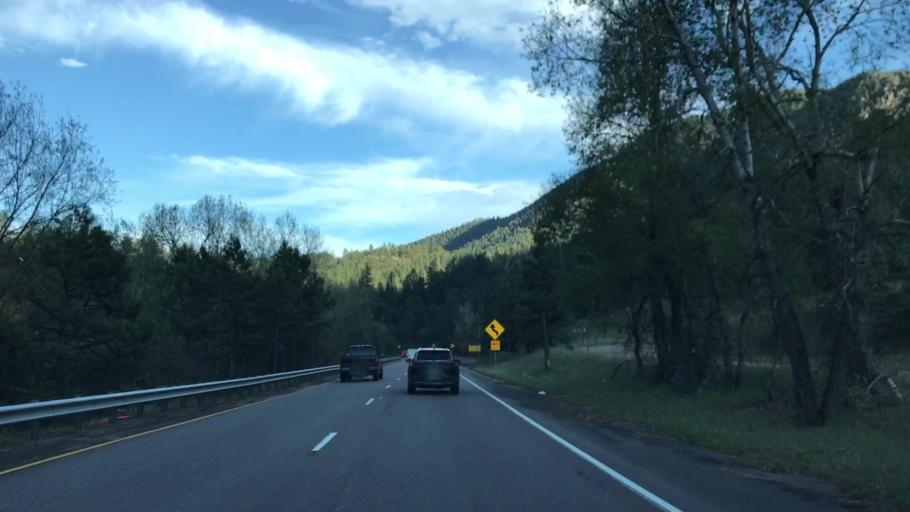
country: US
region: Colorado
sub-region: El Paso County
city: Manitou Springs
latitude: 38.8911
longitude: -104.9661
